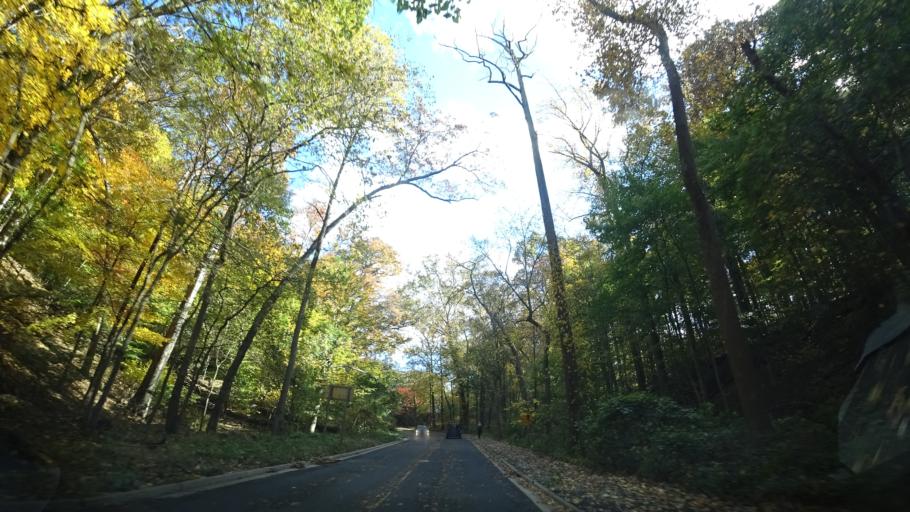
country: US
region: Maryland
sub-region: Montgomery County
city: Chevy Chase
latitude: 38.9430
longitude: -77.0477
